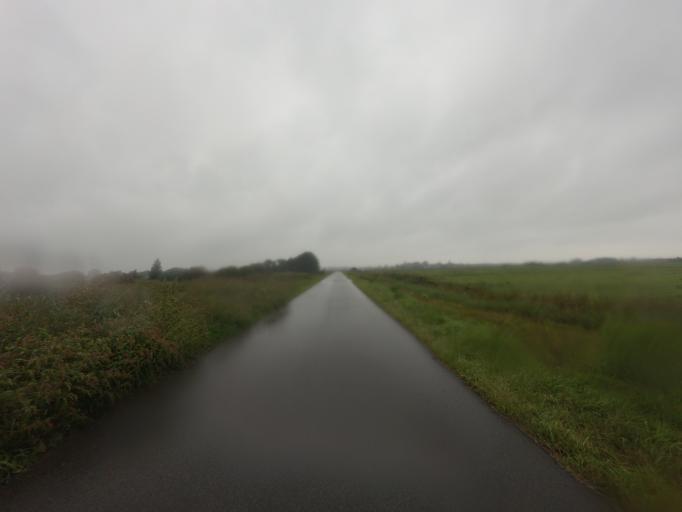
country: NL
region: Friesland
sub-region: Gemeente Smallingerland
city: Oudega
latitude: 53.1022
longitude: 5.9805
